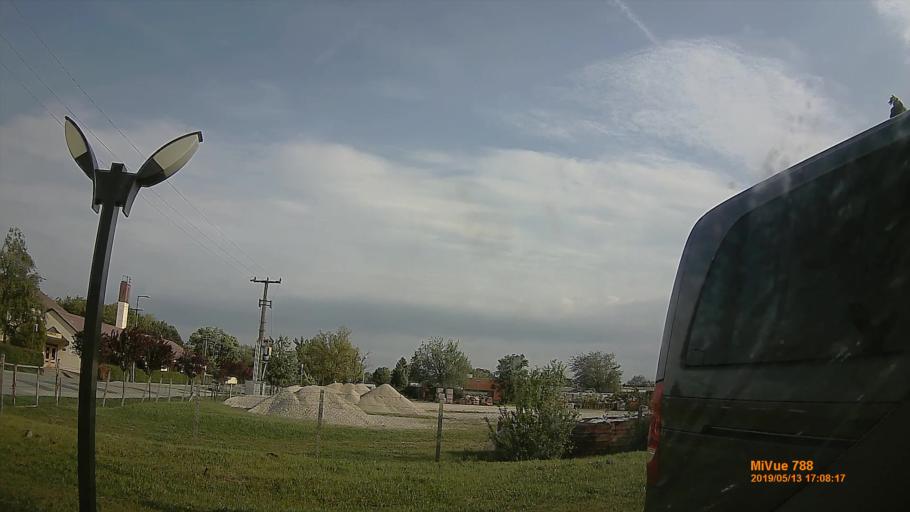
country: HU
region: Veszprem
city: Balatonfured
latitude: 46.9612
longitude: 17.8798
